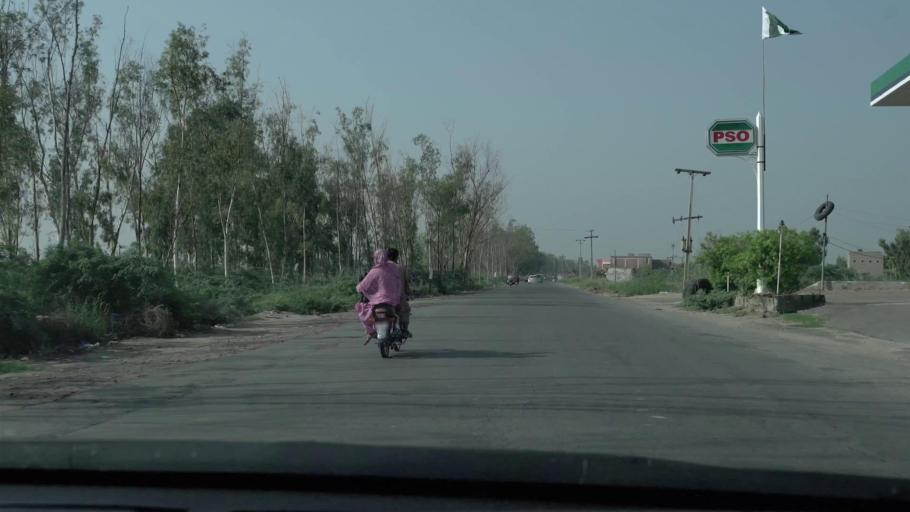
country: PK
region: Punjab
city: Gojra
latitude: 31.1157
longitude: 72.6665
